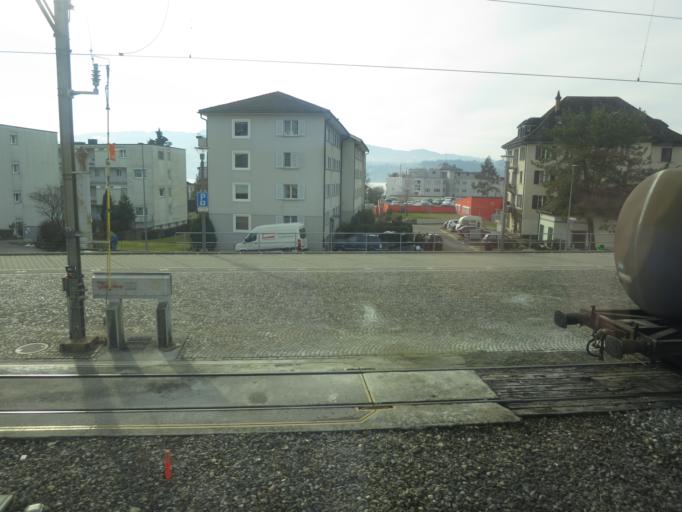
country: CH
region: Zurich
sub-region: Bezirk Meilen
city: Stafa
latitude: 47.2400
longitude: 8.7240
